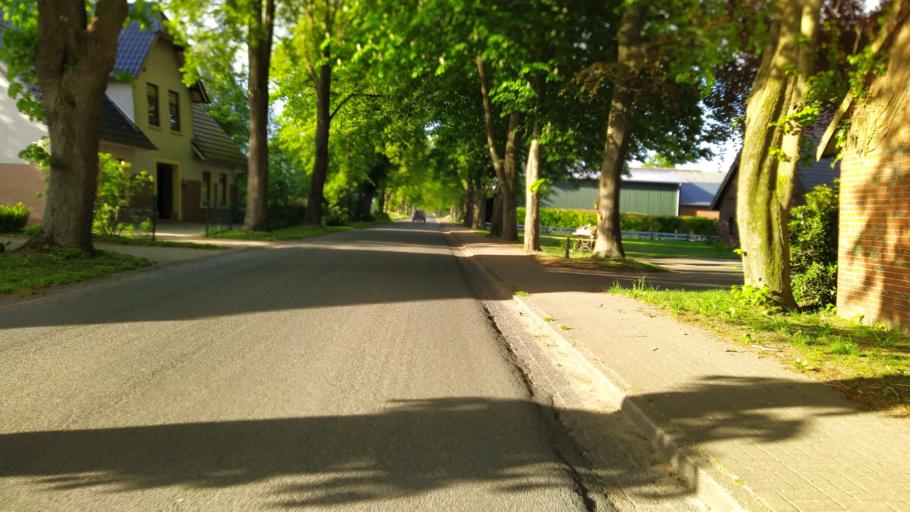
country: DE
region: Lower Saxony
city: Farven
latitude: 53.4158
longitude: 9.3323
